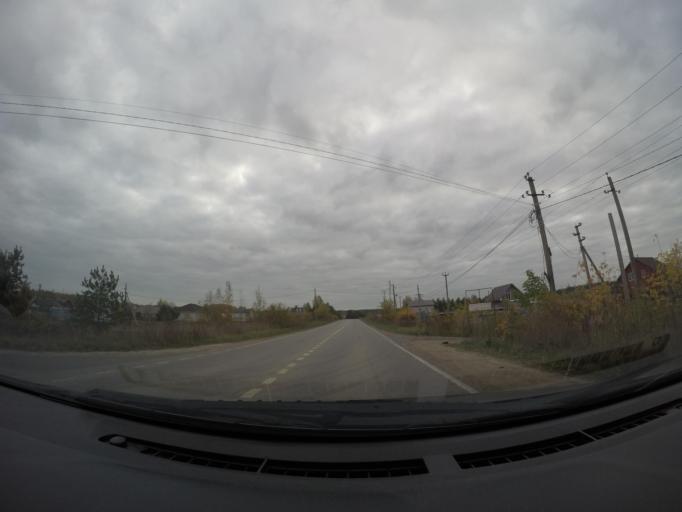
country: RU
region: Moskovskaya
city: Gzhel'
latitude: 55.6438
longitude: 38.4066
